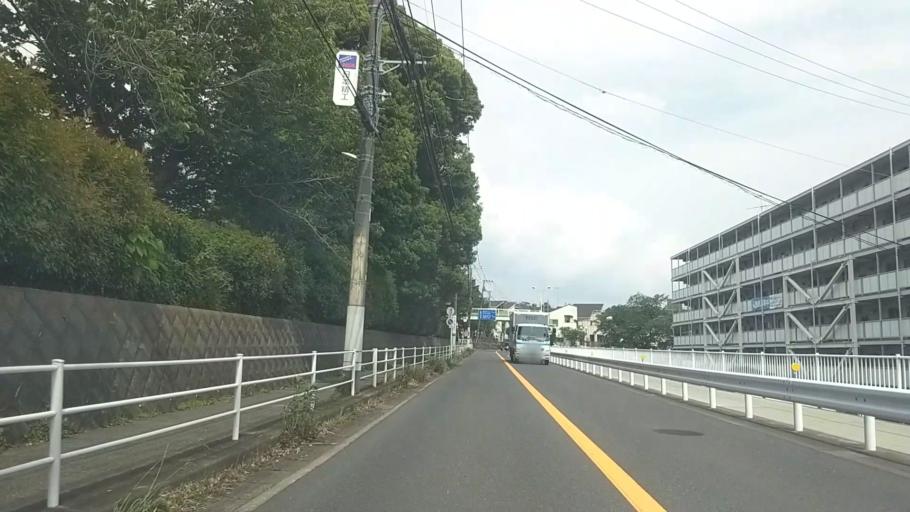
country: JP
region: Kanagawa
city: Fujisawa
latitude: 35.3881
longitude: 139.4642
